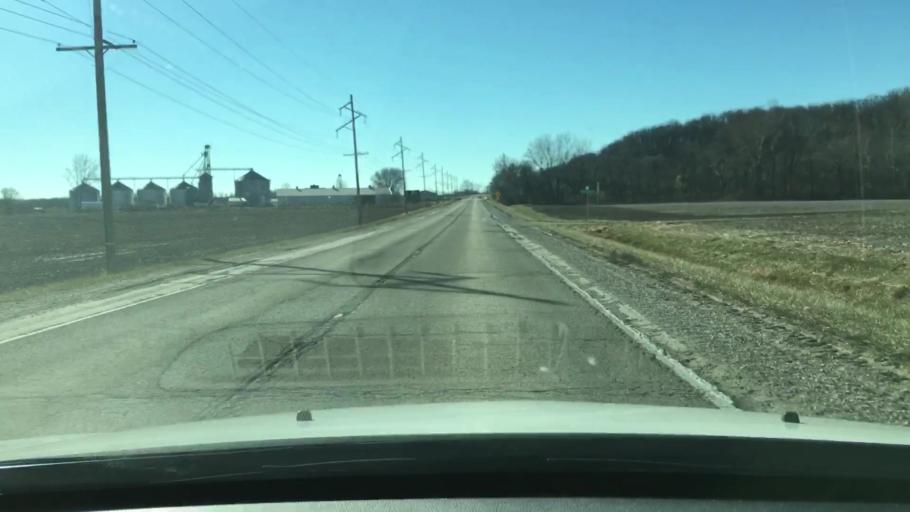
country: US
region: Illinois
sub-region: Fulton County
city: Astoria
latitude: 40.1699
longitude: -90.2910
